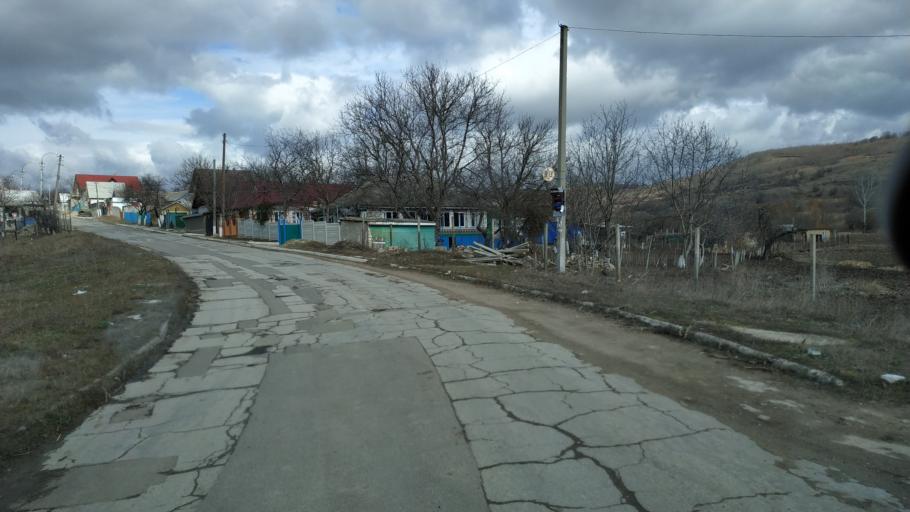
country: MD
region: Stinga Nistrului
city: Bucovat
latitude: 47.2046
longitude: 28.4975
